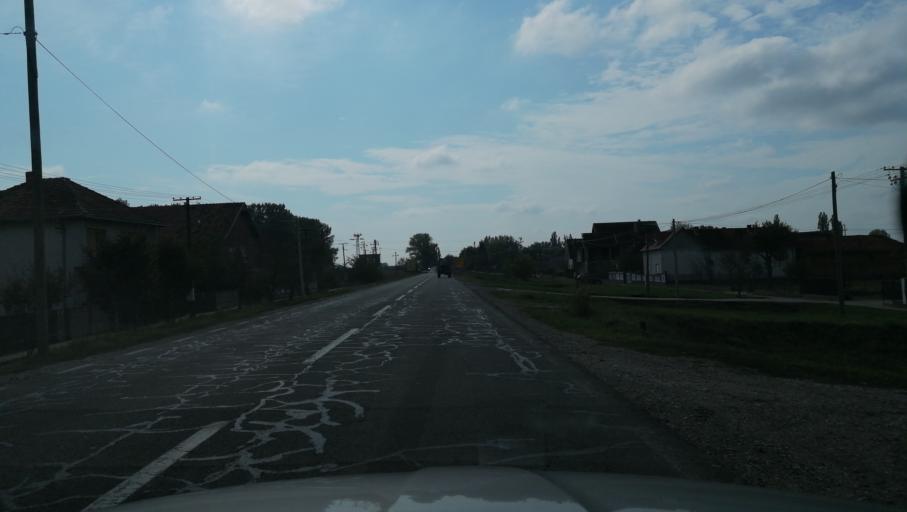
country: RS
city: Bosut
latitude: 44.9475
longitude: 19.3699
